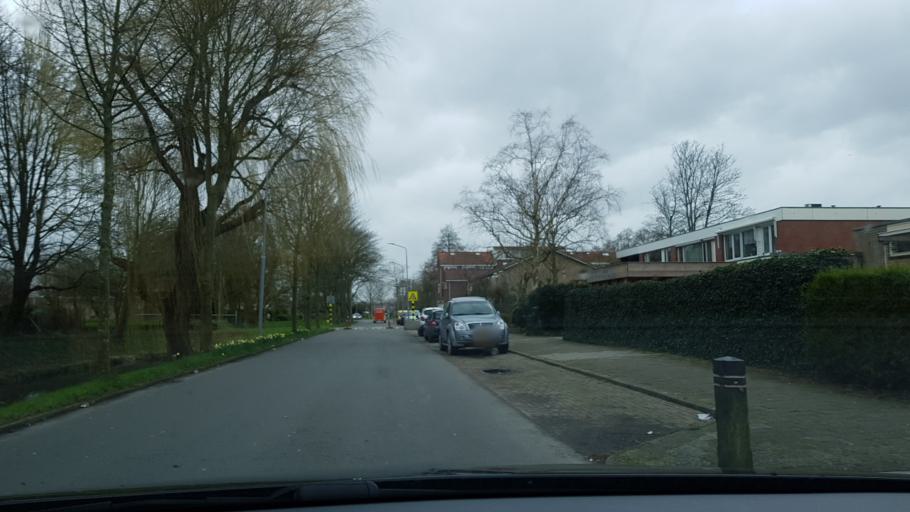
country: NL
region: North Holland
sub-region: Gemeente Haarlemmermeer
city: Hoofddorp
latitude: 52.3127
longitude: 4.6892
